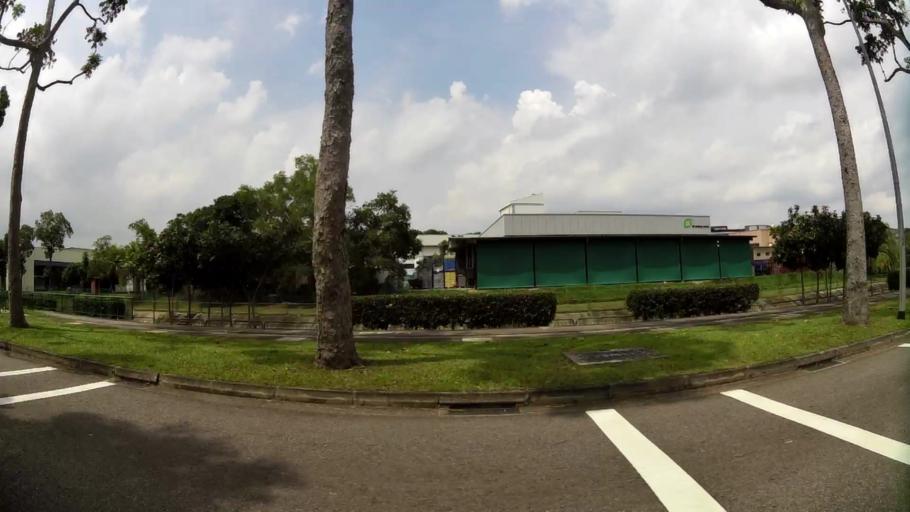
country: MY
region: Johor
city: Kampung Pasir Gudang Baru
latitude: 1.3771
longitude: 103.9779
